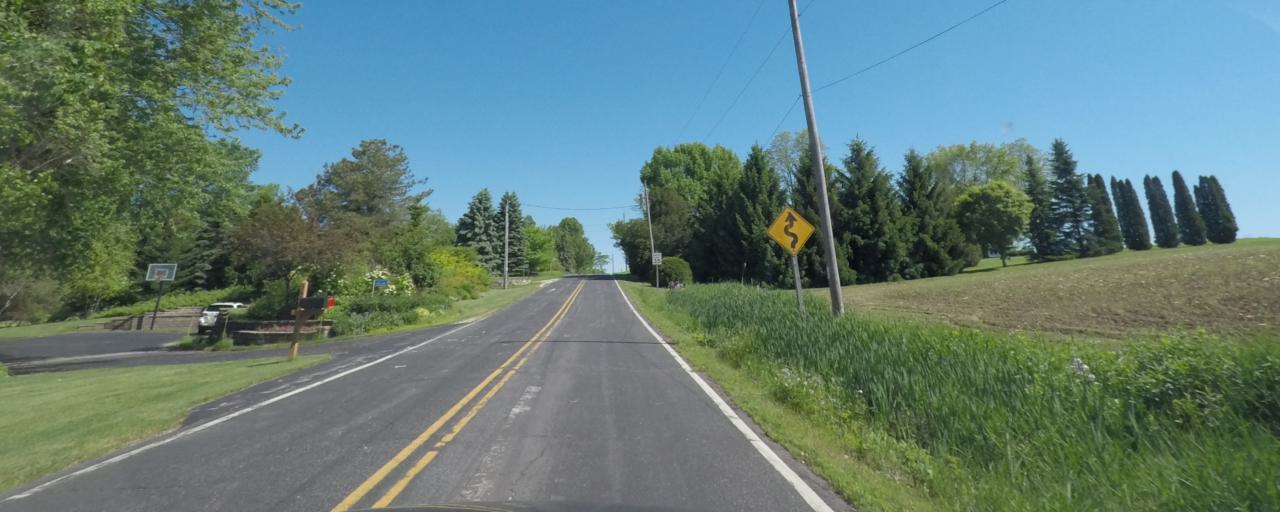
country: US
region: Wisconsin
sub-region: Sheboygan County
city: Sheboygan Falls
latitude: 43.7452
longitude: -87.8402
